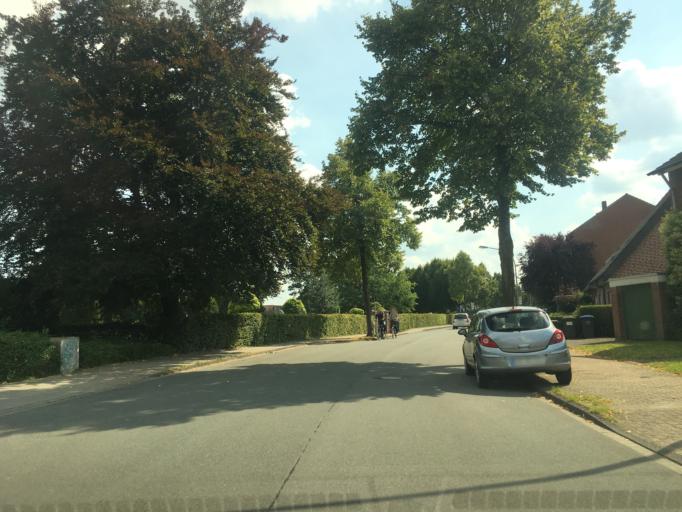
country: DE
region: North Rhine-Westphalia
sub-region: Regierungsbezirk Munster
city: Muenster
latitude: 51.8813
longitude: 7.6083
